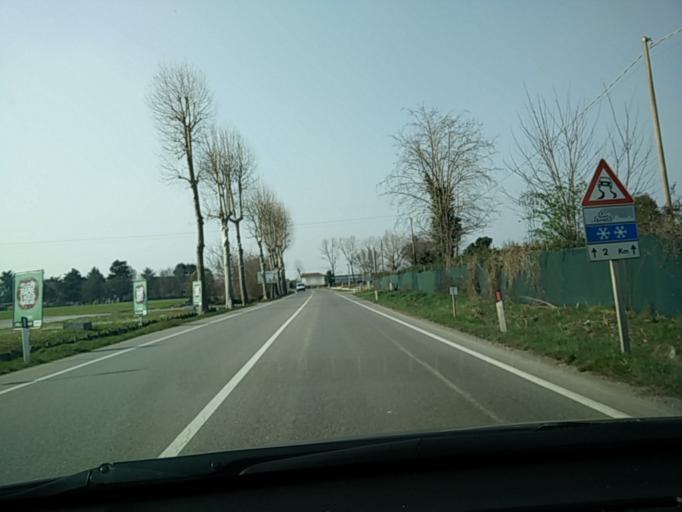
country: IT
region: Veneto
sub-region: Provincia di Treviso
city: Castagnole
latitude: 45.7059
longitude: 12.1729
